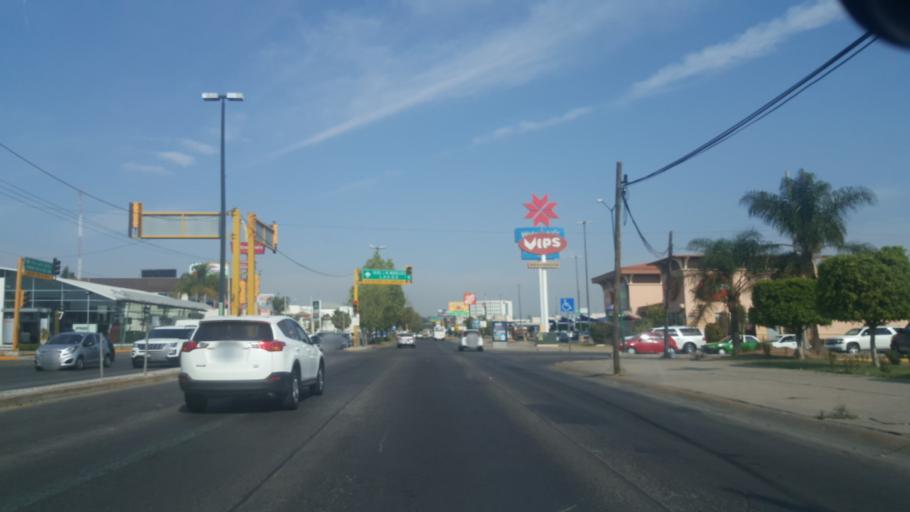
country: MX
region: Guanajuato
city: Leon
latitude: 21.1597
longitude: -101.6920
